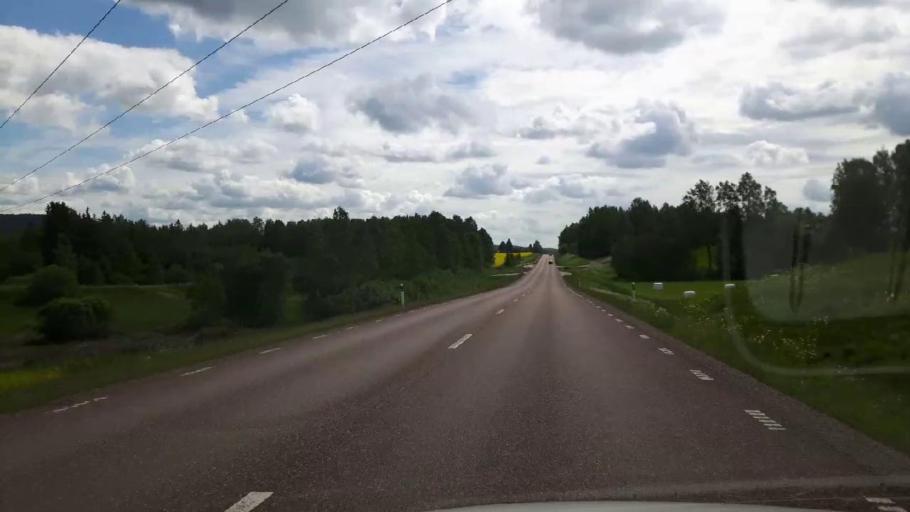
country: SE
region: Dalarna
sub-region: Hedemora Kommun
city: Langshyttan
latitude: 60.3830
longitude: 15.9075
